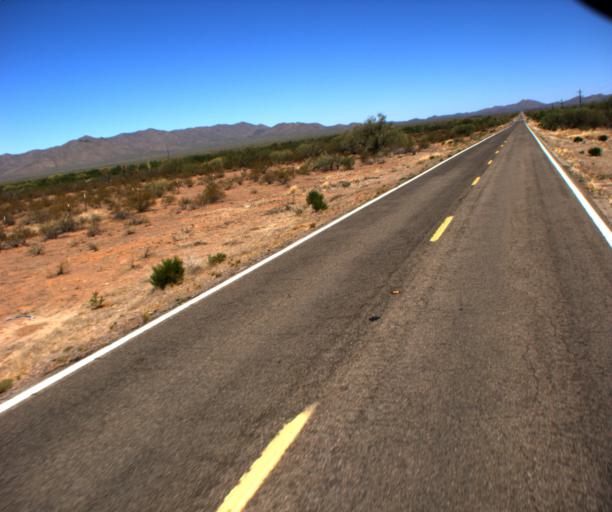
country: US
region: Arizona
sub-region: Pima County
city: Sells
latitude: 32.0850
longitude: -112.0533
